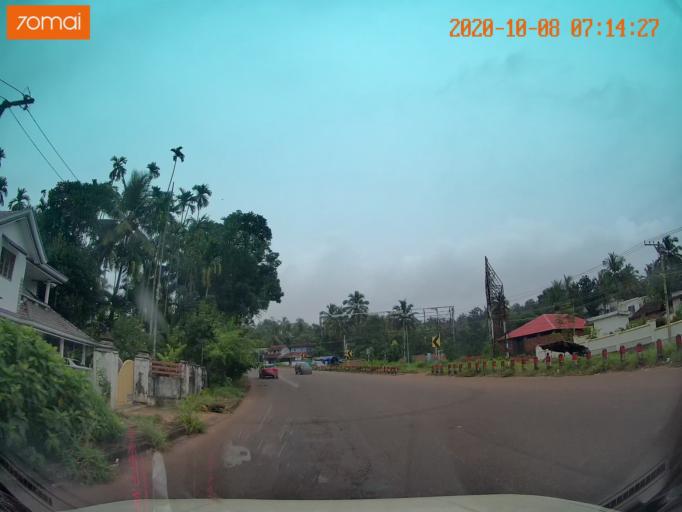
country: IN
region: Kerala
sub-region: Malappuram
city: Ponnani
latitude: 10.8173
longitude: 76.0187
